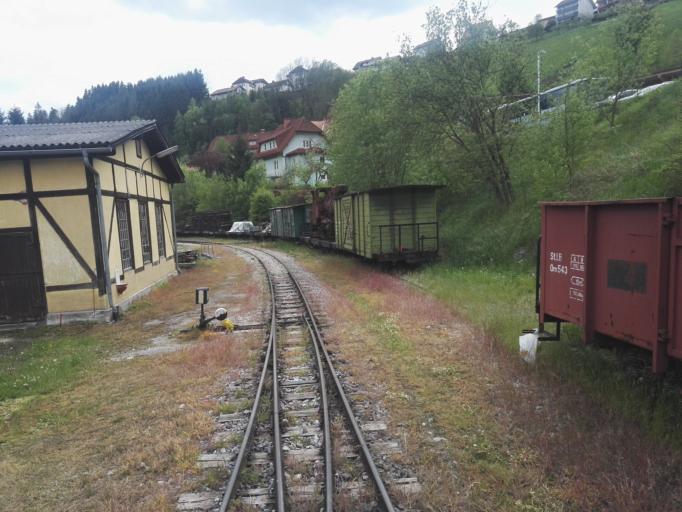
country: AT
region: Styria
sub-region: Politischer Bezirk Weiz
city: Birkfeld
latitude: 47.3515
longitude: 15.6969
